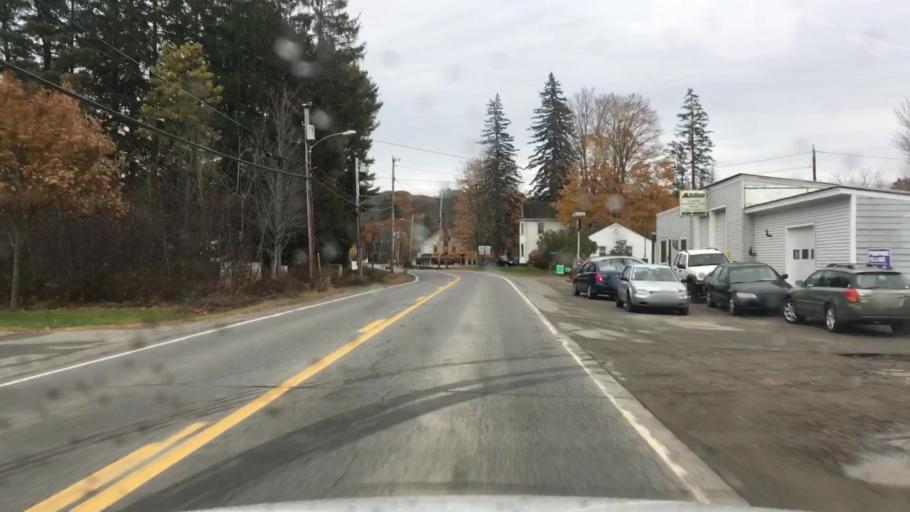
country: US
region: Maine
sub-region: Lincoln County
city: Jefferson
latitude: 44.2013
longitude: -69.4579
